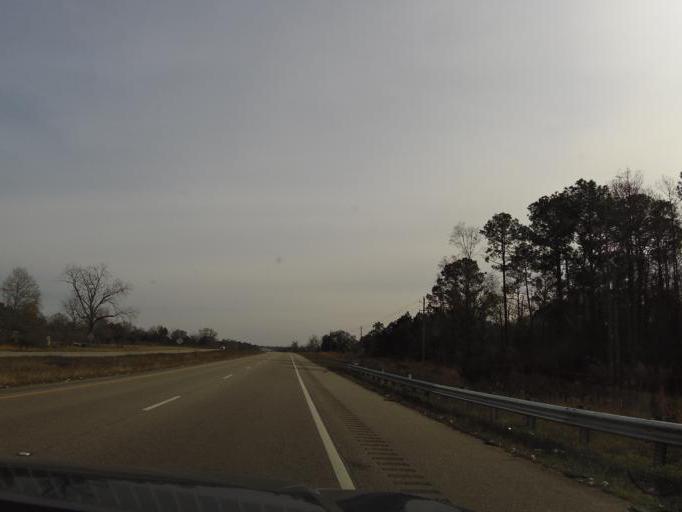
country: US
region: Alabama
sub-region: Houston County
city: Ashford
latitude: 31.1569
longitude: -85.1840
